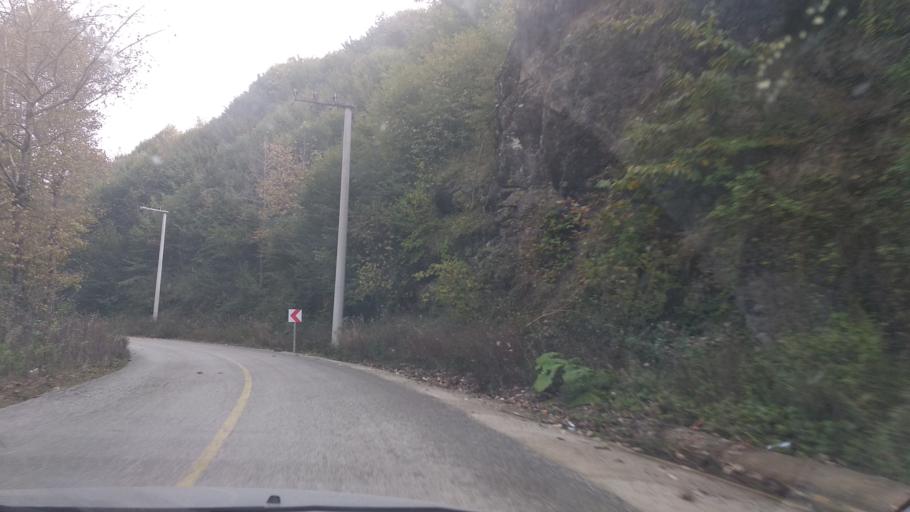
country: TR
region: Duzce
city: Kaynasli
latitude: 40.7332
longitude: 31.2214
